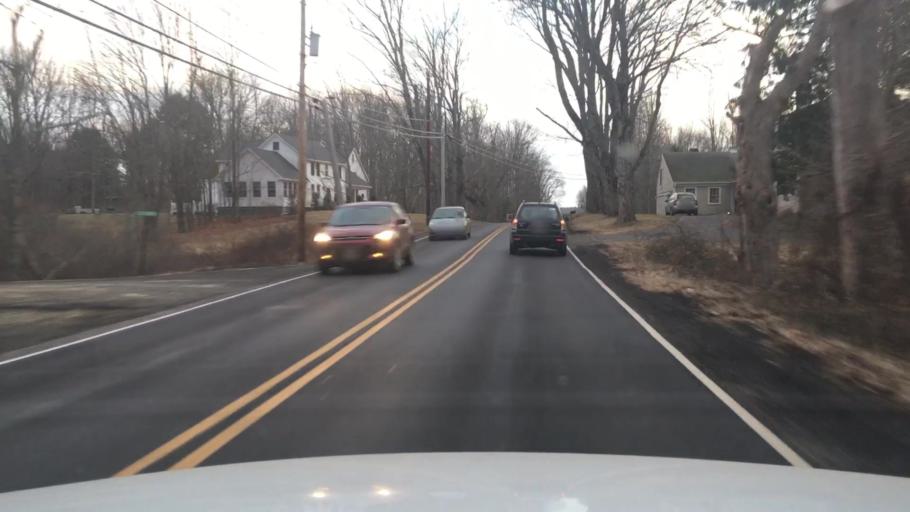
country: US
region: Maine
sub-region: Lincoln County
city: Damariscotta
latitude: 44.0068
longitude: -69.5305
